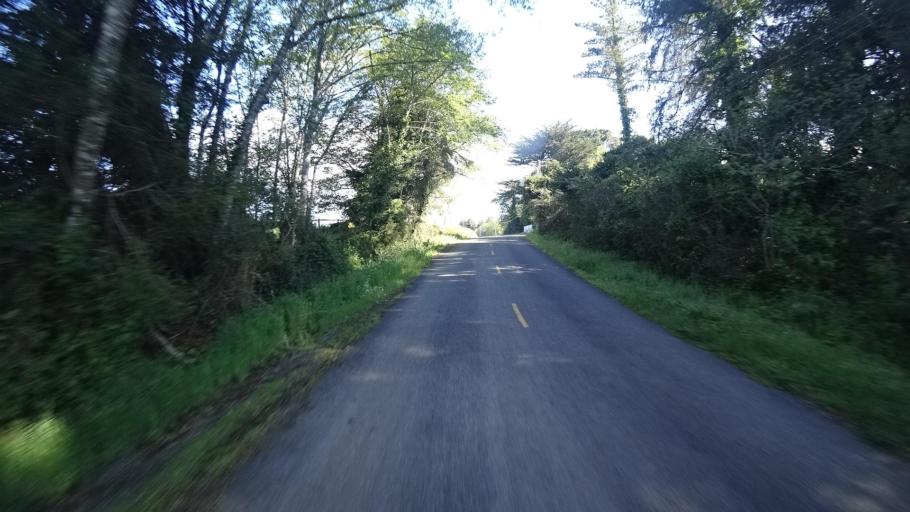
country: US
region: California
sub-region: Humboldt County
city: Westhaven-Moonstone
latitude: 40.9993
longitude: -124.1007
